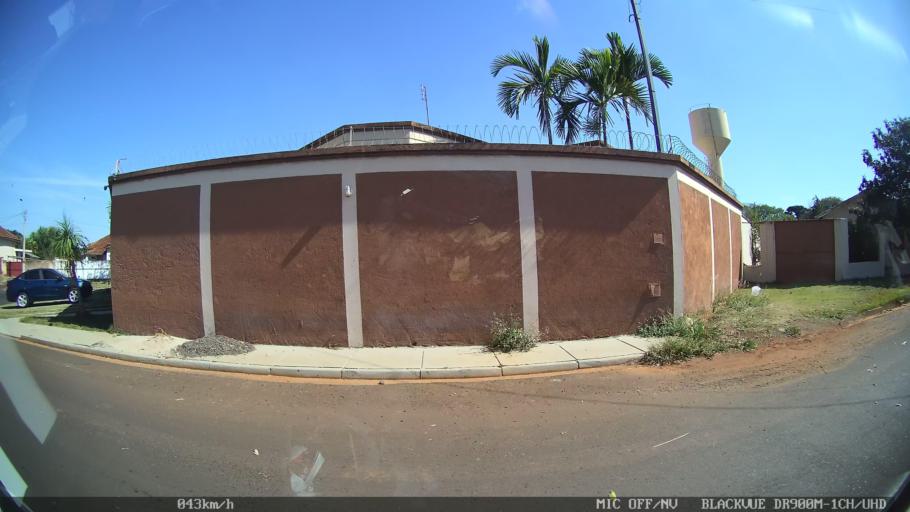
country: BR
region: Sao Paulo
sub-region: Batatais
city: Batatais
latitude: -20.8815
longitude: -47.6023
